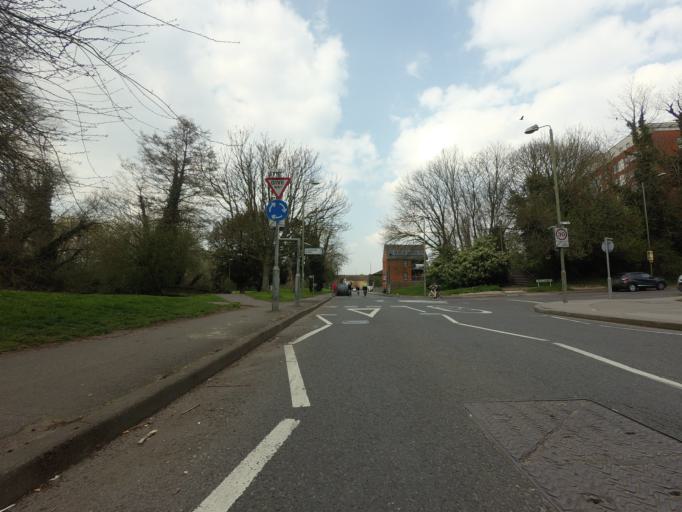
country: GB
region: England
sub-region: Greater London
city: Orpington
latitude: 51.3918
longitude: 0.1147
